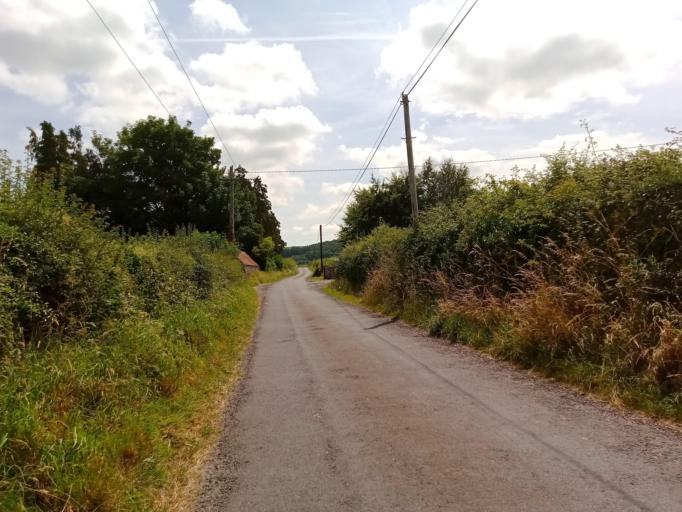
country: IE
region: Leinster
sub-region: Laois
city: Rathdowney
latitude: 52.8122
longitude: -7.4699
